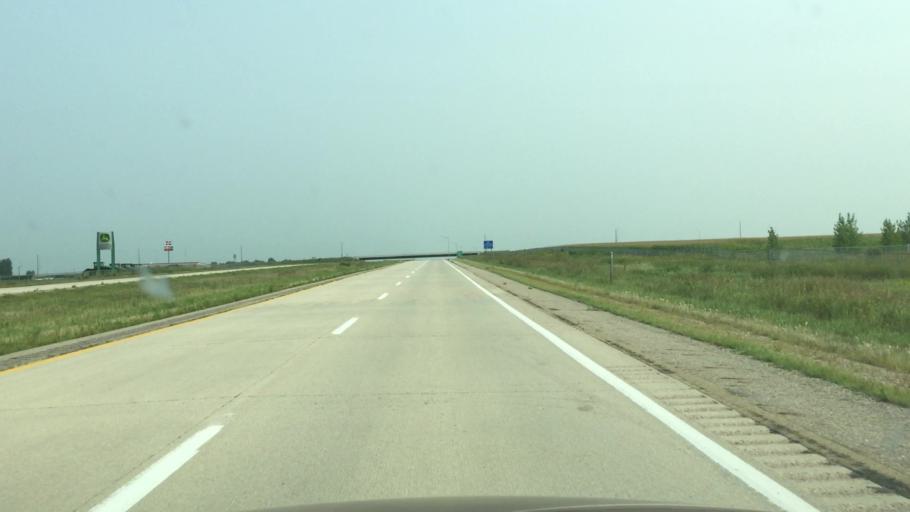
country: US
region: Iowa
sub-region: Osceola County
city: Sibley
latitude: 43.3983
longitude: -95.7171
